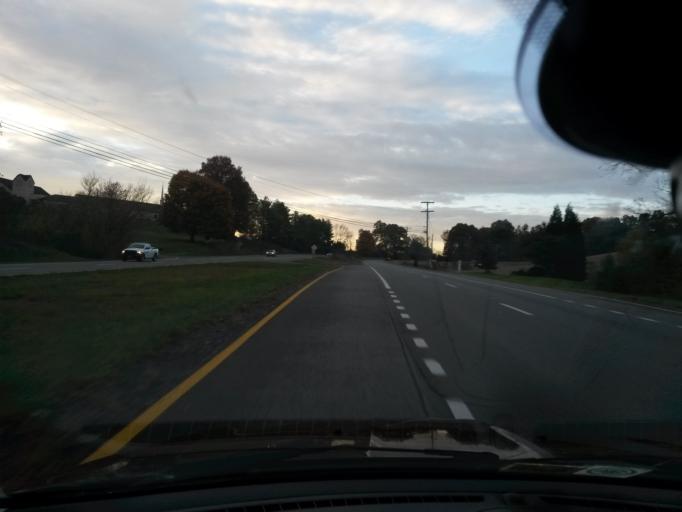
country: US
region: Virginia
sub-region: Botetourt County
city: Fincastle
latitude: 37.4855
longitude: -79.8788
